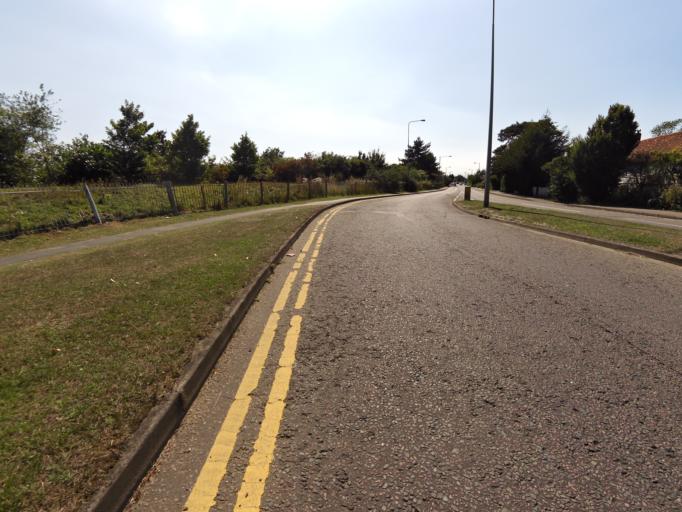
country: GB
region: England
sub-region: Essex
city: Eight Ash Green
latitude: 51.8868
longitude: 0.8332
